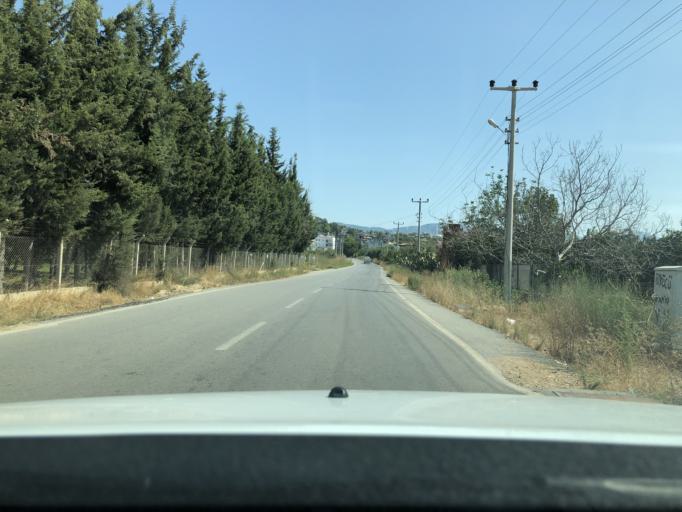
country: TR
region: Antalya
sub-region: Manavgat
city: Manavgat
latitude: 36.8072
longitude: 31.4797
